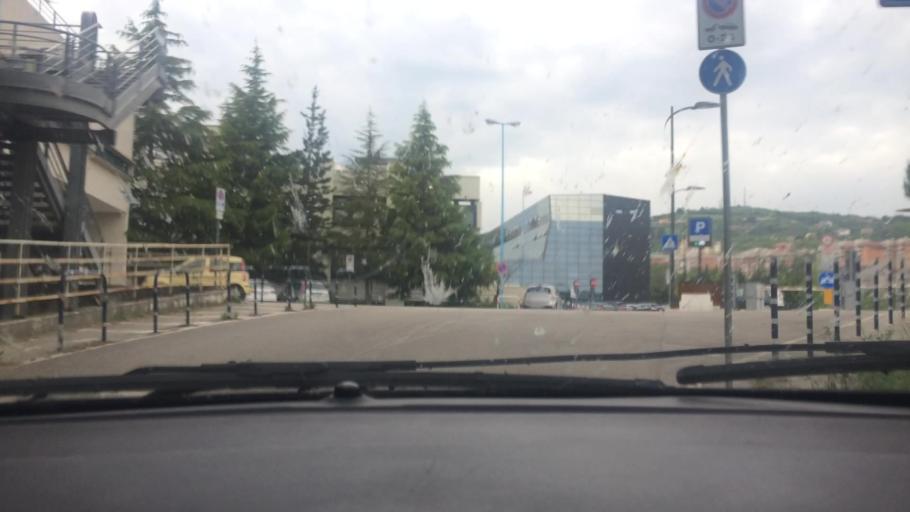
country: IT
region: Basilicate
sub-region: Provincia di Potenza
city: Potenza
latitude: 40.6521
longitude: 15.8080
